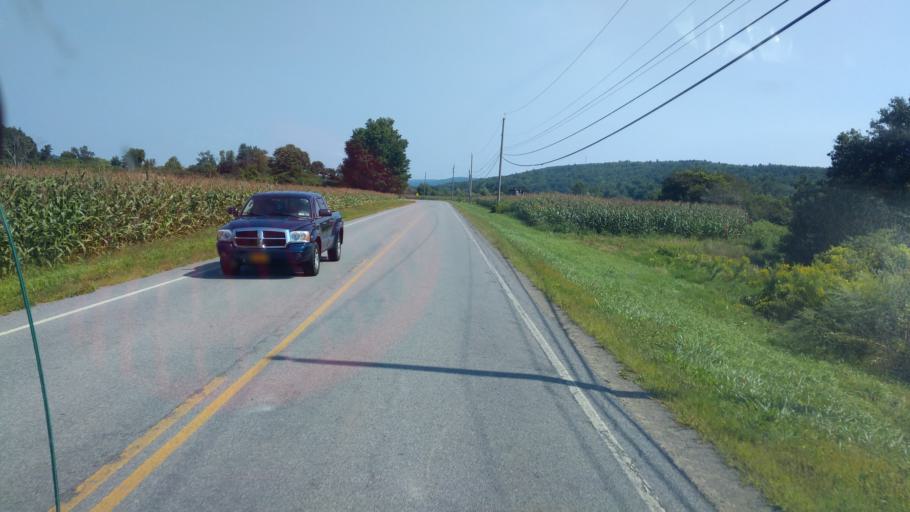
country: US
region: New York
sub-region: Allegany County
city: Friendship
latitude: 42.2262
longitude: -78.0908
